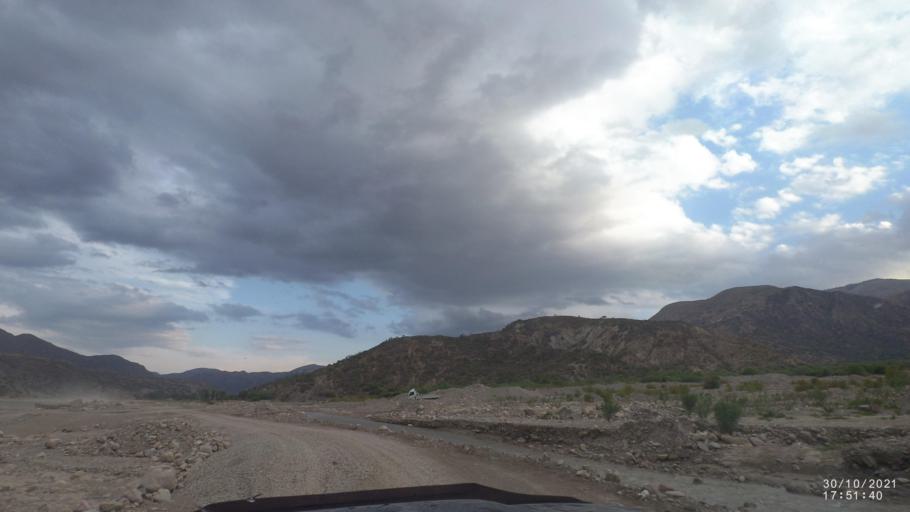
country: BO
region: Cochabamba
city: Sipe Sipe
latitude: -17.5368
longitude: -66.5038
